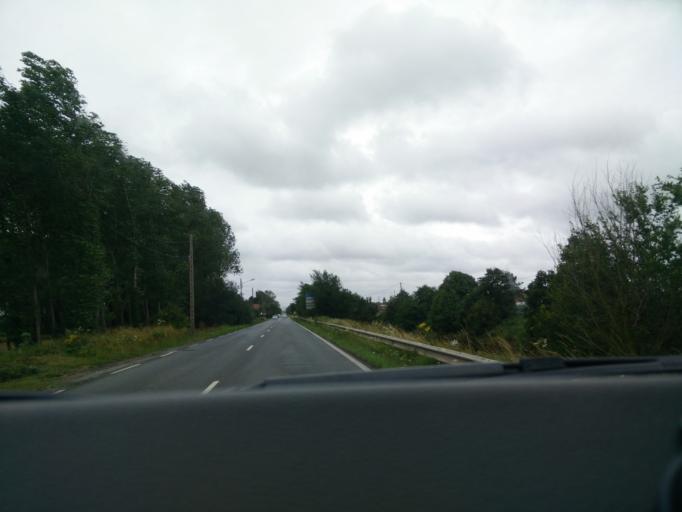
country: FR
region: Nord-Pas-de-Calais
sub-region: Departement du Nord
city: Teteghem
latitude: 51.0408
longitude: 2.4299
